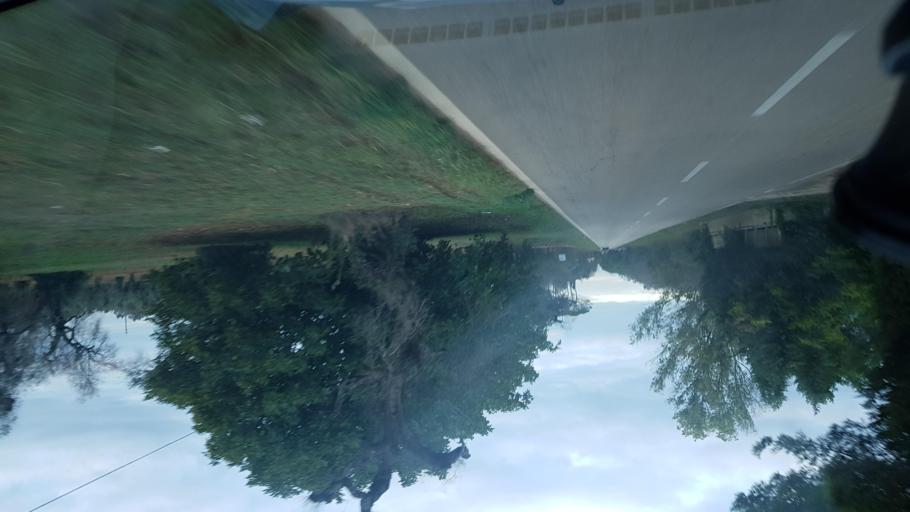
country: IT
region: Apulia
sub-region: Provincia di Brindisi
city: Oria
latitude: 40.5122
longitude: 17.6658
